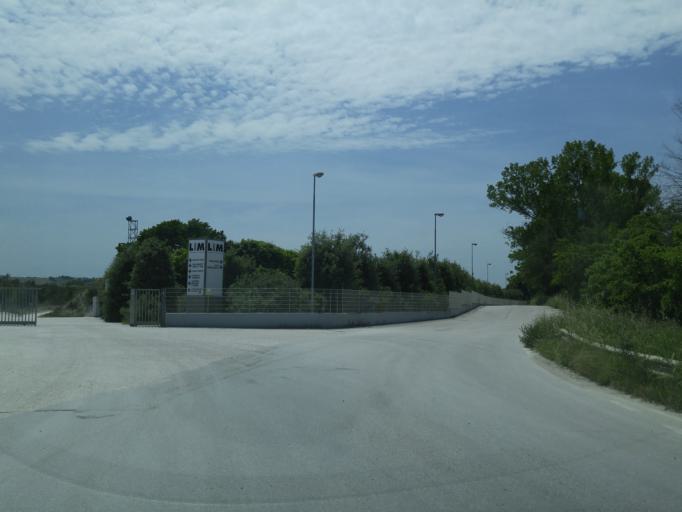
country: IT
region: The Marches
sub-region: Provincia di Pesaro e Urbino
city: Bellocchi
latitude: 43.7872
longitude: 13.0134
